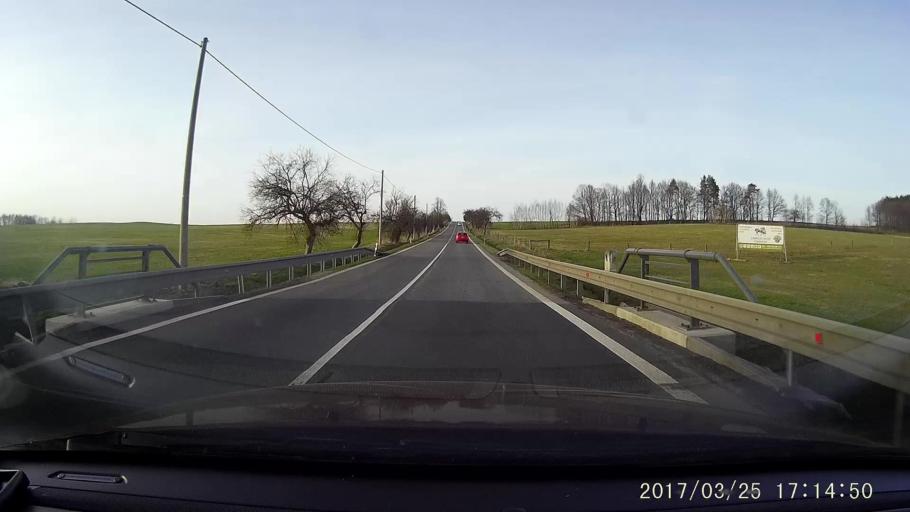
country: CZ
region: Liberecky
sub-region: Okres Liberec
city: Frydlant
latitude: 50.9363
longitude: 15.0952
